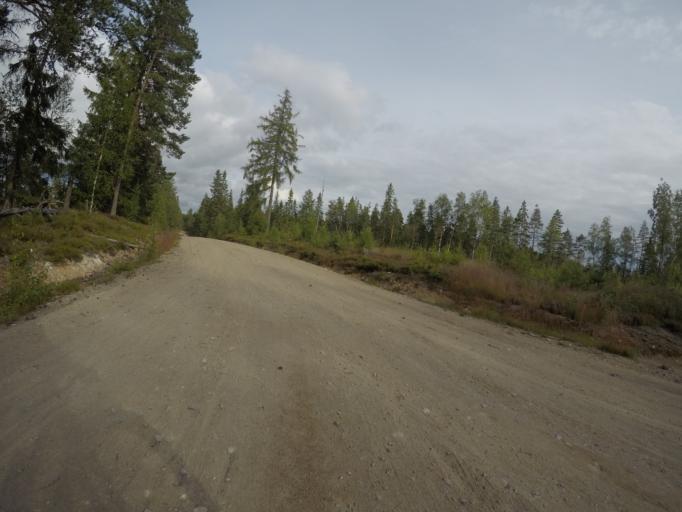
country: SE
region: Vaermland
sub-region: Filipstads Kommun
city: Lesjofors
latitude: 60.1984
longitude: 14.3178
